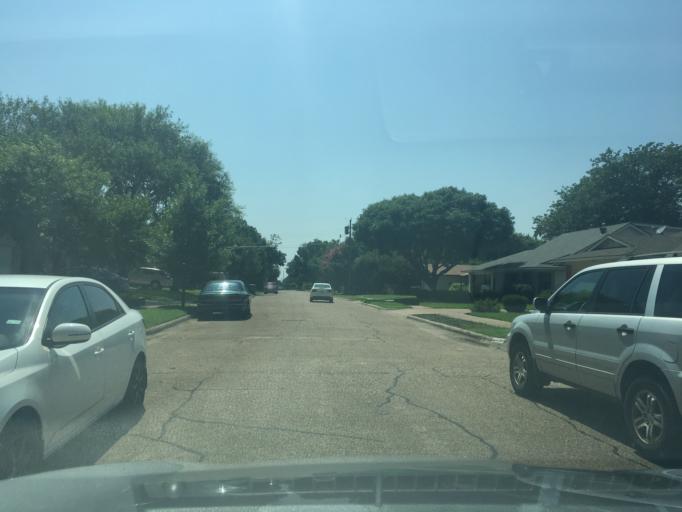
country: US
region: Texas
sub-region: Dallas County
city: Richardson
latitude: 32.9276
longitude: -96.7039
